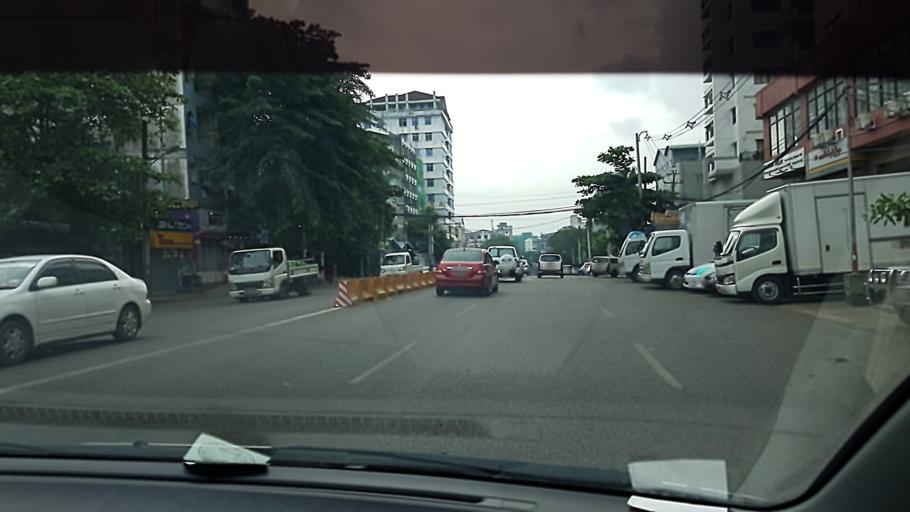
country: MM
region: Yangon
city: Yangon
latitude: 16.7985
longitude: 96.1262
